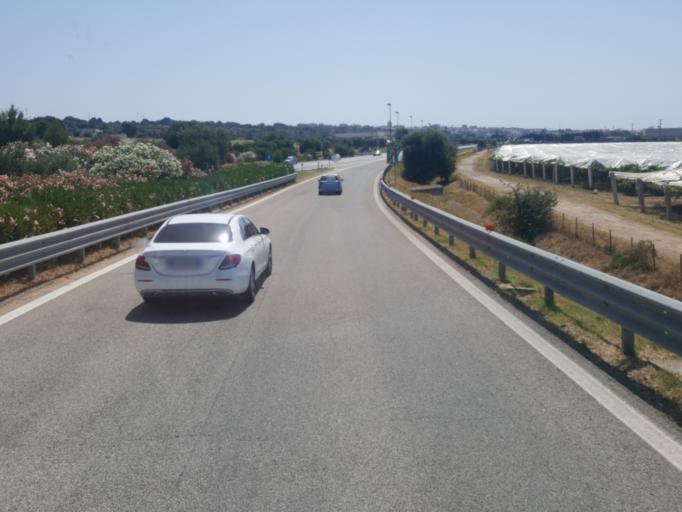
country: IT
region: Apulia
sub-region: Provincia di Taranto
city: Massafra
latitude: 40.5964
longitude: 17.0839
